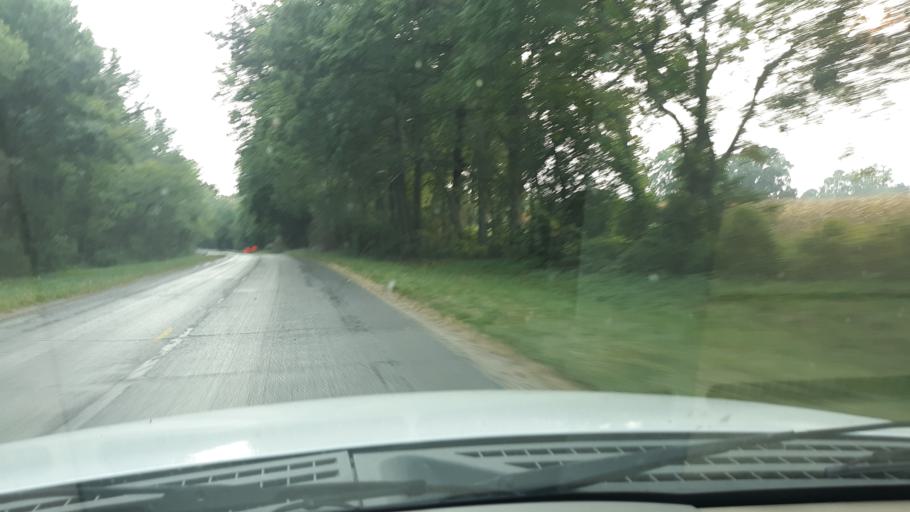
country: US
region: Illinois
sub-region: Edwards County
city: Grayville
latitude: 38.2888
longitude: -87.9775
